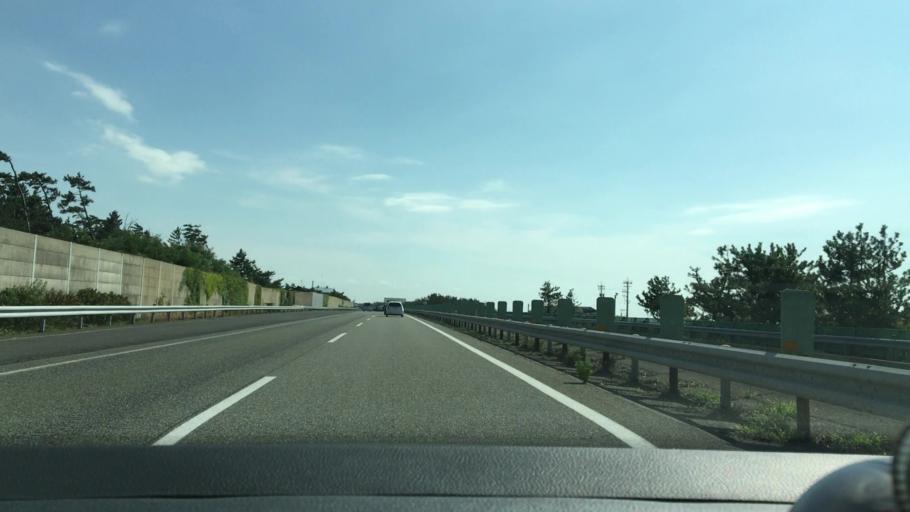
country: JP
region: Ishikawa
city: Komatsu
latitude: 36.4572
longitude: 136.4537
